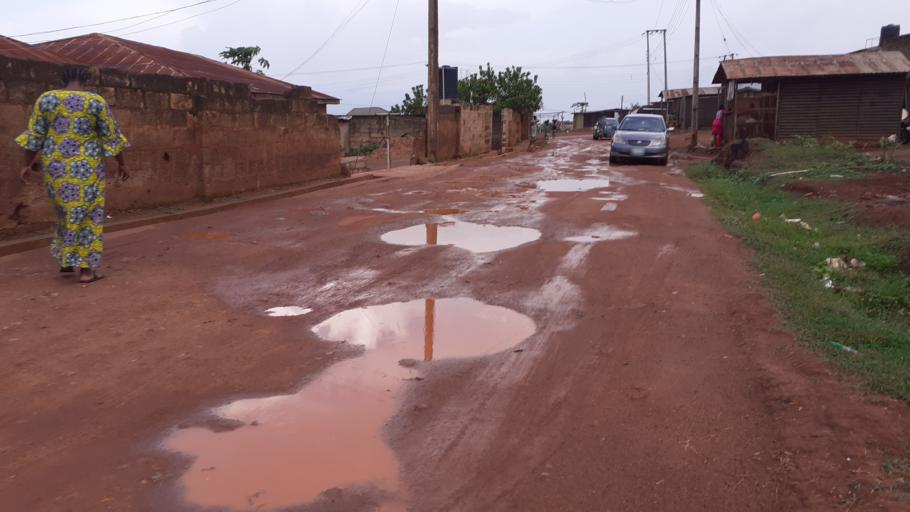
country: NG
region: Ondo
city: Akure
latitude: 7.2139
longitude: 5.2176
